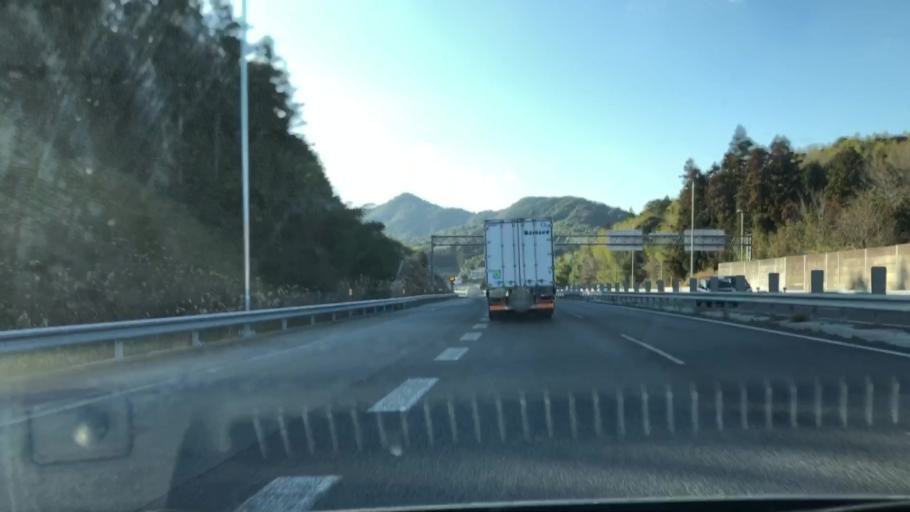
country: JP
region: Yamaguchi
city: Ogori-shimogo
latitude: 34.1726
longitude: 131.3192
